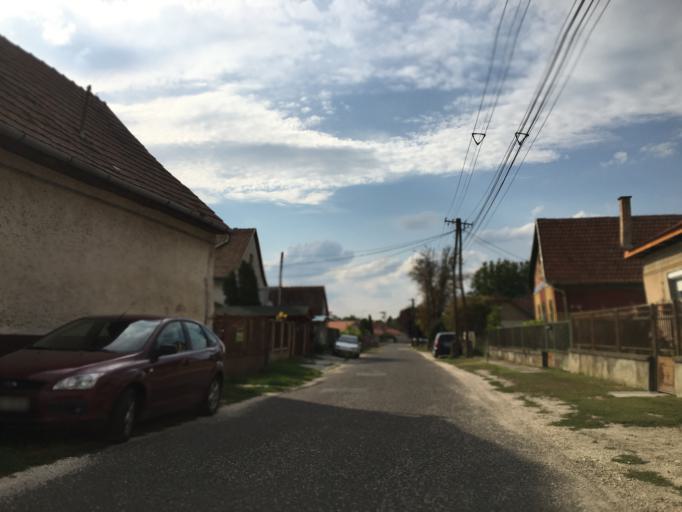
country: HU
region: Pest
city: Szigetszentmiklos
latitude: 47.3519
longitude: 19.0478
